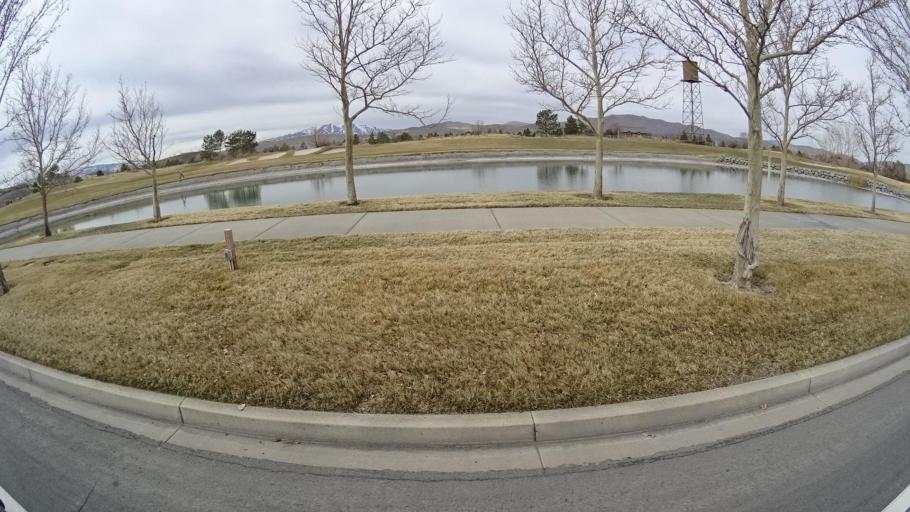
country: US
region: Nevada
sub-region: Washoe County
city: Spanish Springs
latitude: 39.6101
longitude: -119.6870
